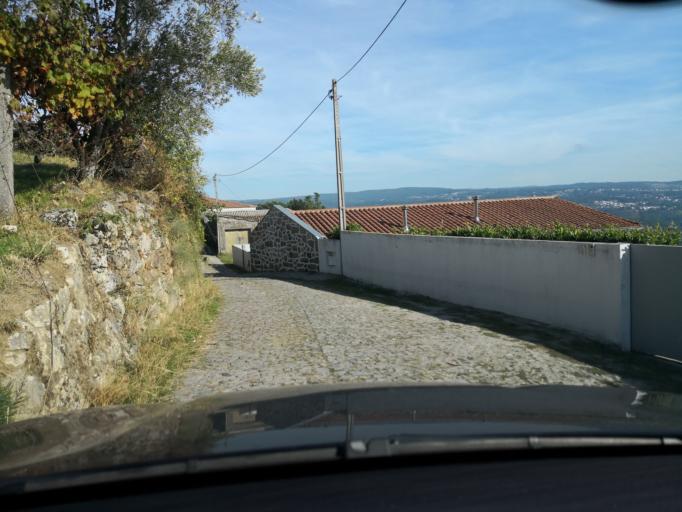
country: PT
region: Vila Real
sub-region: Vila Real
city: Vila Real
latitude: 41.3368
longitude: -7.7495
